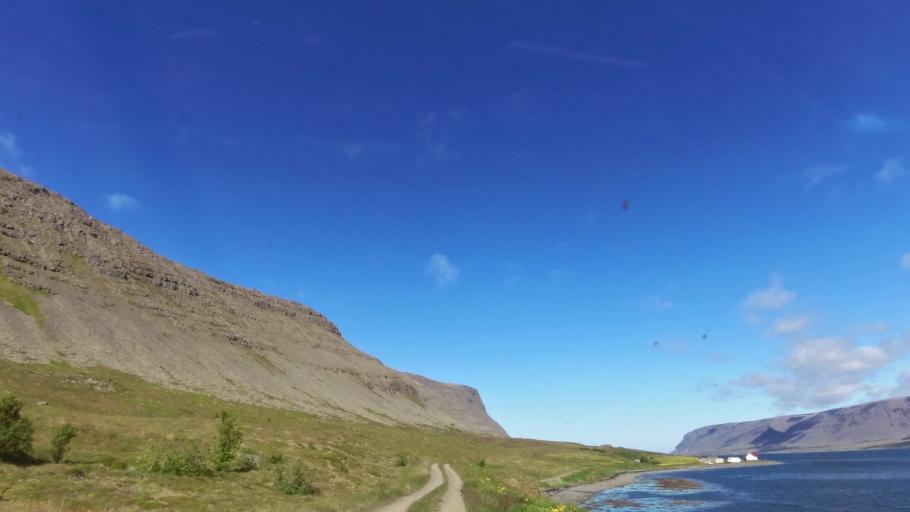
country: IS
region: West
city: Olafsvik
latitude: 65.6181
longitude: -23.8621
